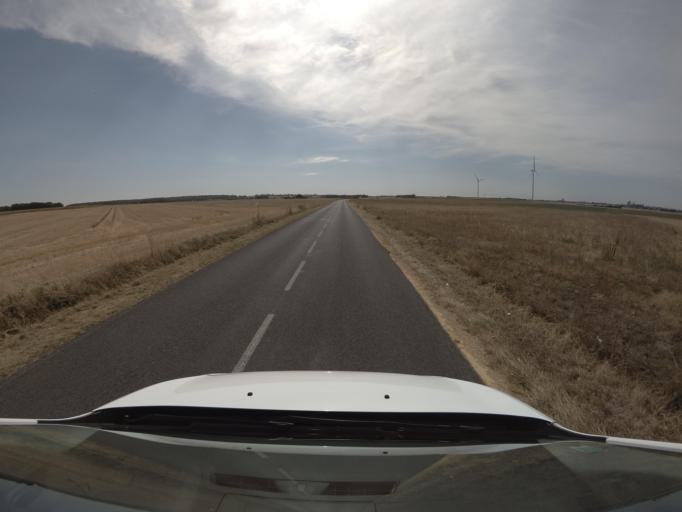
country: FR
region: Poitou-Charentes
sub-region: Departement des Deux-Sevres
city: Saint-Leger-de-Montbrun
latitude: 46.9891
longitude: -0.1565
